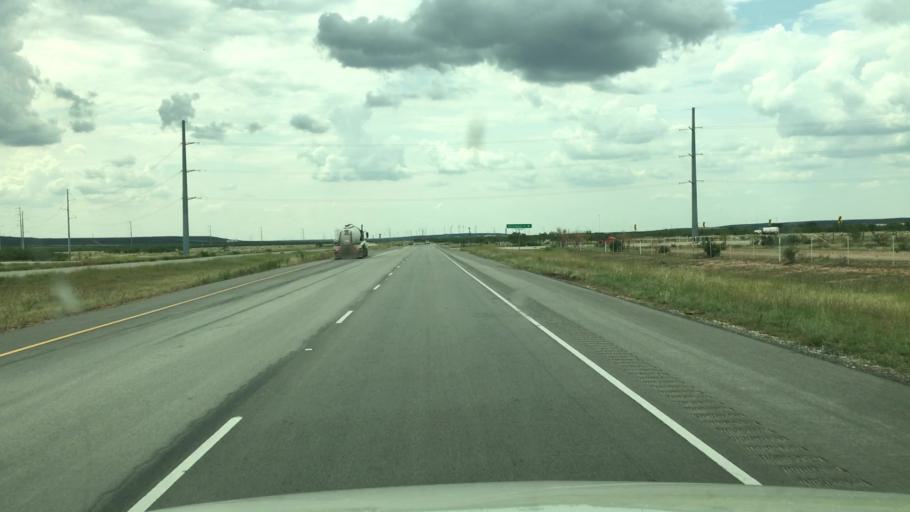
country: US
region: Texas
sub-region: Sterling County
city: Sterling City
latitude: 31.9605
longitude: -101.2116
